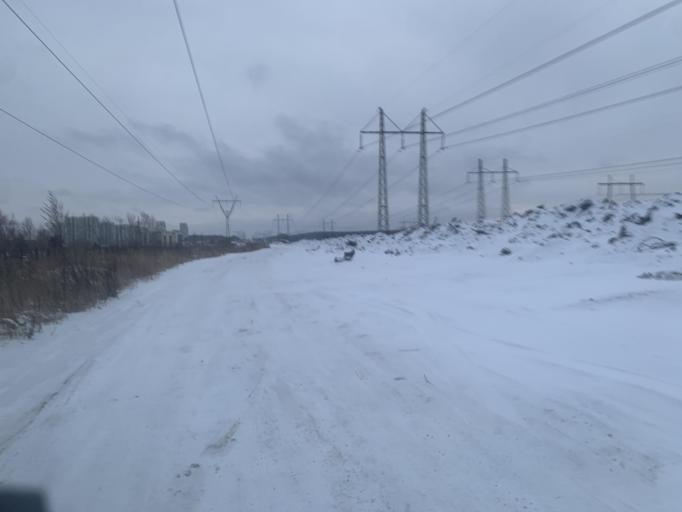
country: RU
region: Chelyabinsk
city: Roshchino
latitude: 55.1867
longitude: 61.2578
